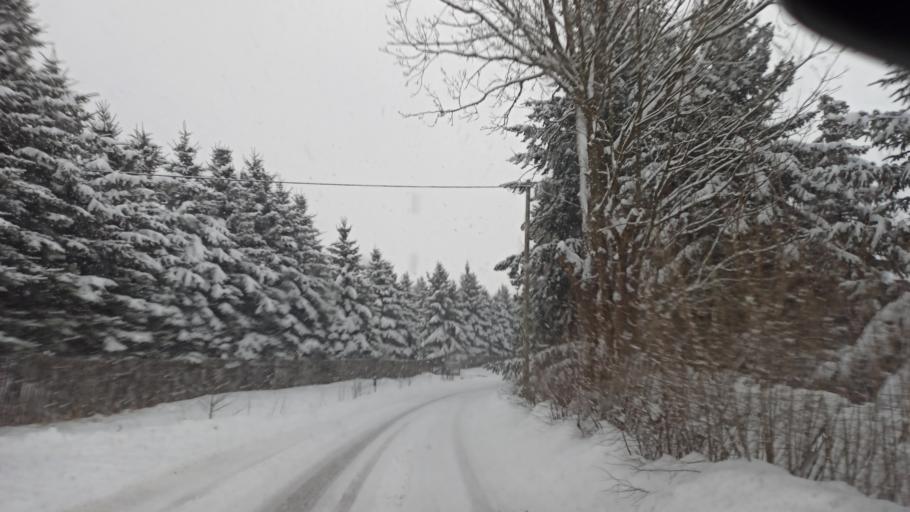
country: PL
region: Lower Silesian Voivodeship
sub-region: Powiat klodzki
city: Ludwikowice Klodzkie
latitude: 50.6487
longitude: 16.4803
